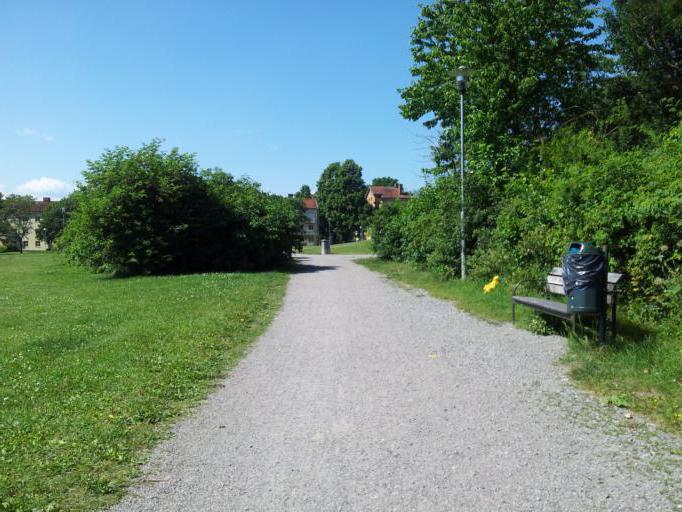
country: SE
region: Uppsala
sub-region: Uppsala Kommun
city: Uppsala
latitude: 59.8693
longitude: 17.6750
